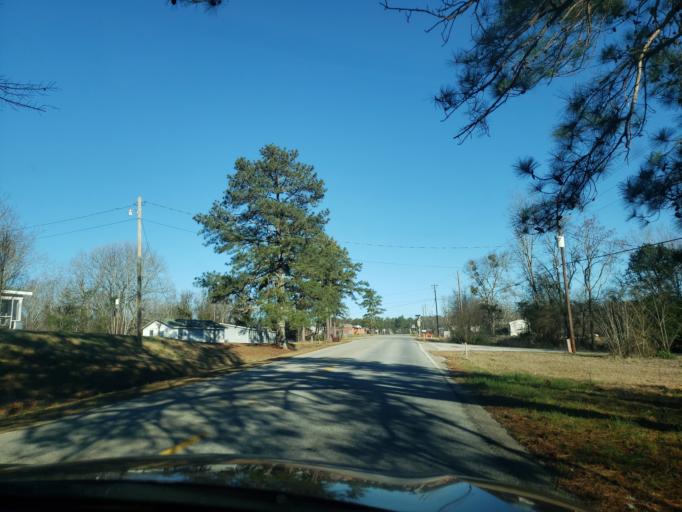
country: US
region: Alabama
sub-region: Elmore County
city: Tallassee
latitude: 32.6002
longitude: -85.8026
